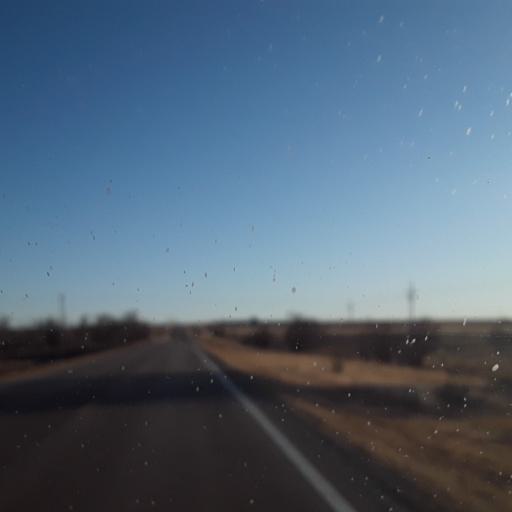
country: US
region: Kansas
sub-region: Wallace County
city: Sharon Springs
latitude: 38.9396
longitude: -101.7492
